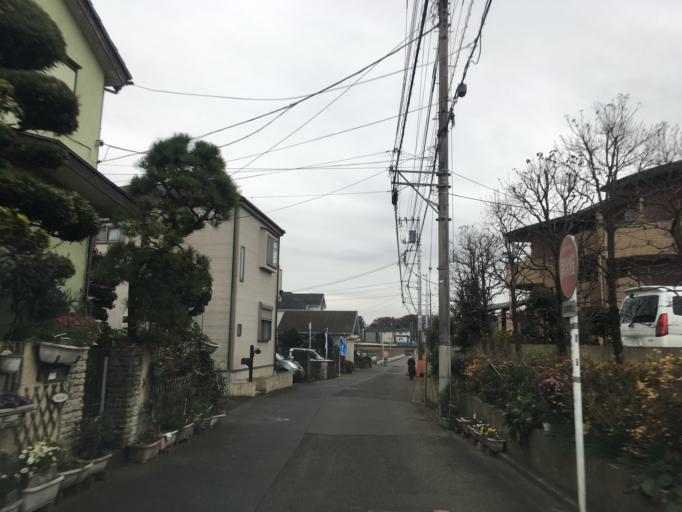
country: JP
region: Tokyo
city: Higashimurayama-shi
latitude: 35.7492
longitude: 139.4858
